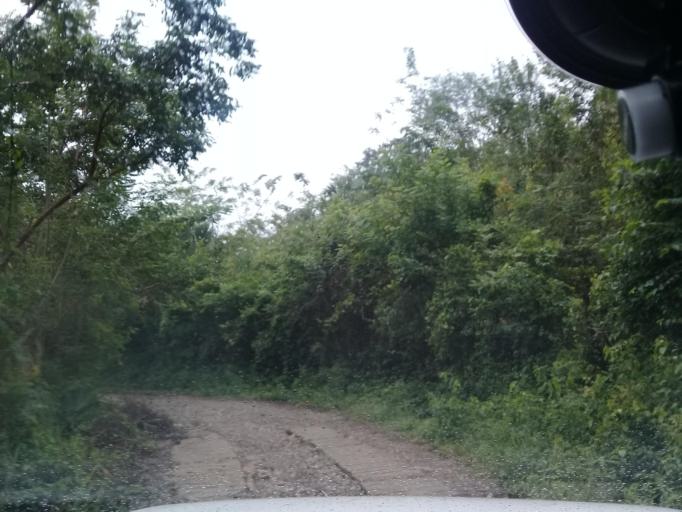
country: MX
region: Veracruz
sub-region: Chalma
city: San Pedro Coyutla
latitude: 21.2440
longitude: -98.4196
